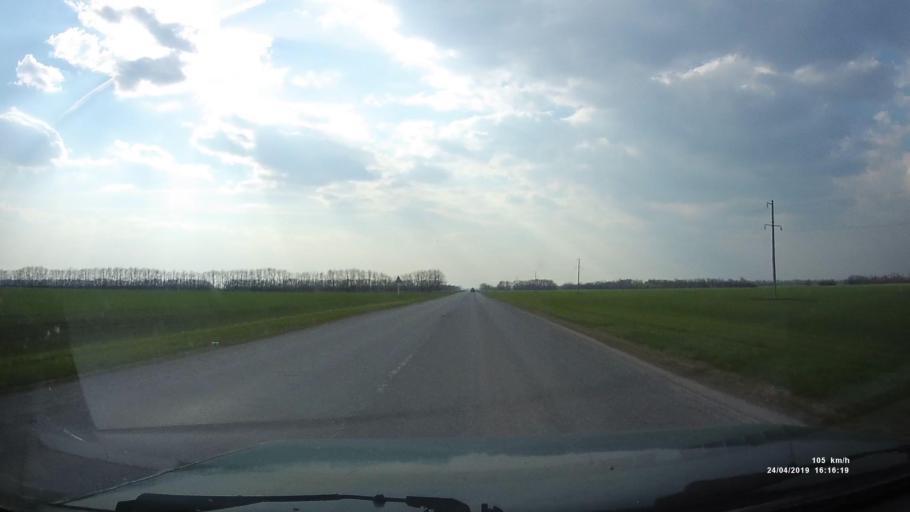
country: RU
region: Rostov
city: Sovetskoye
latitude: 46.7624
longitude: 42.1623
